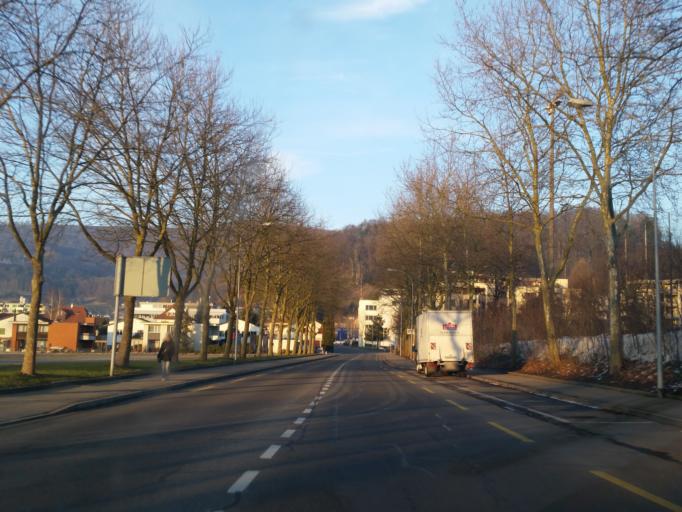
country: CH
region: Aargau
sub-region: Bezirk Baden
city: Neuenhof
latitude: 47.4592
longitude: 8.3352
